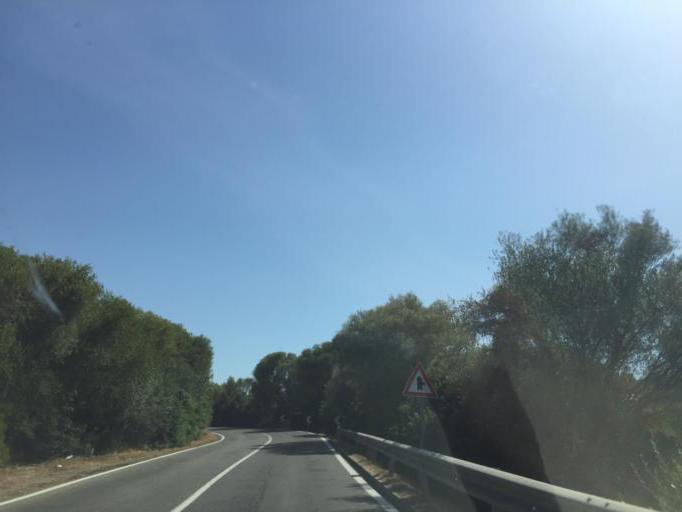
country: IT
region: Sardinia
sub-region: Provincia di Olbia-Tempio
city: San Teodoro
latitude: 40.7709
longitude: 9.6545
